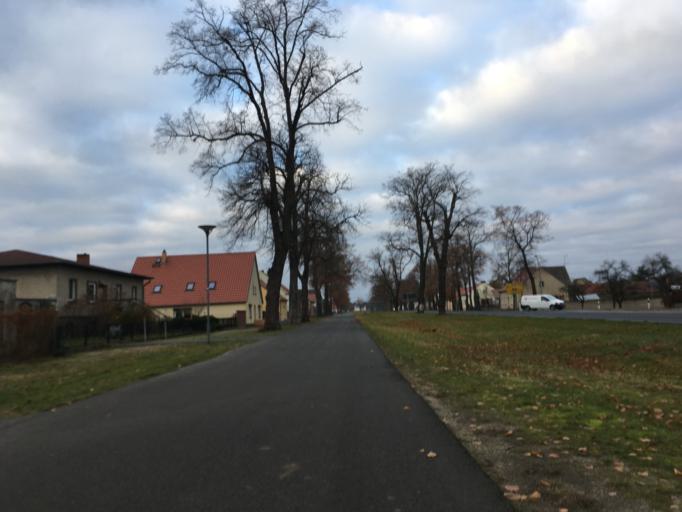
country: DE
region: Brandenburg
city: Neuhardenberg
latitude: 52.5928
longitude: 14.2574
